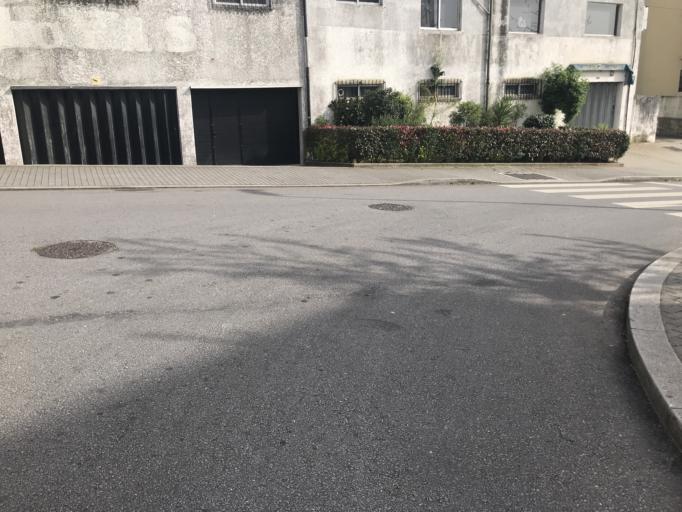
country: PT
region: Porto
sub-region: Matosinhos
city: Matosinhos
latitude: 41.1744
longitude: -8.6733
